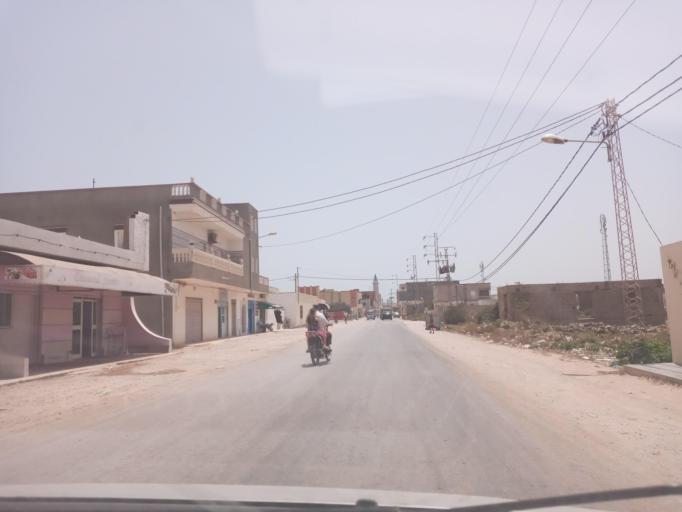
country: TN
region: Nabul
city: El Haouaria
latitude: 37.0137
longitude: 10.9516
